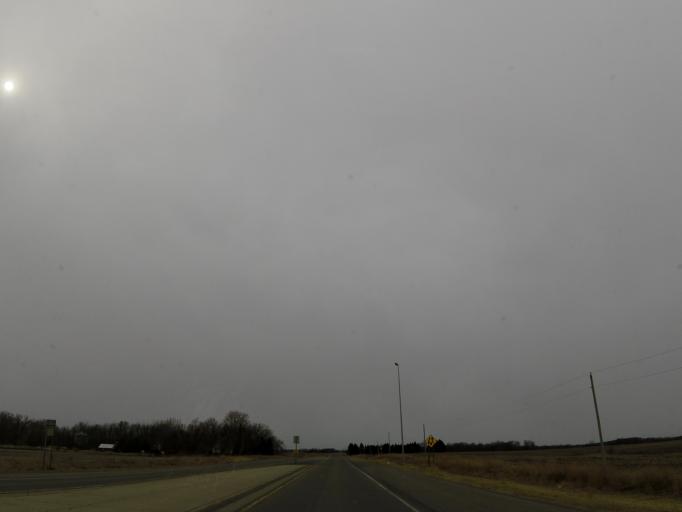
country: US
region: Minnesota
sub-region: Le Sueur County
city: Le Sueur
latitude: 44.5431
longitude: -93.8567
